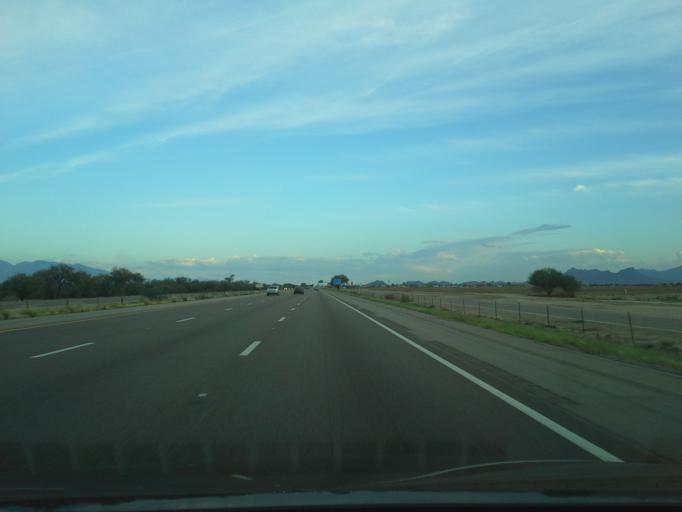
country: US
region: Arizona
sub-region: Pima County
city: Marana
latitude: 32.4751
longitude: -111.2350
